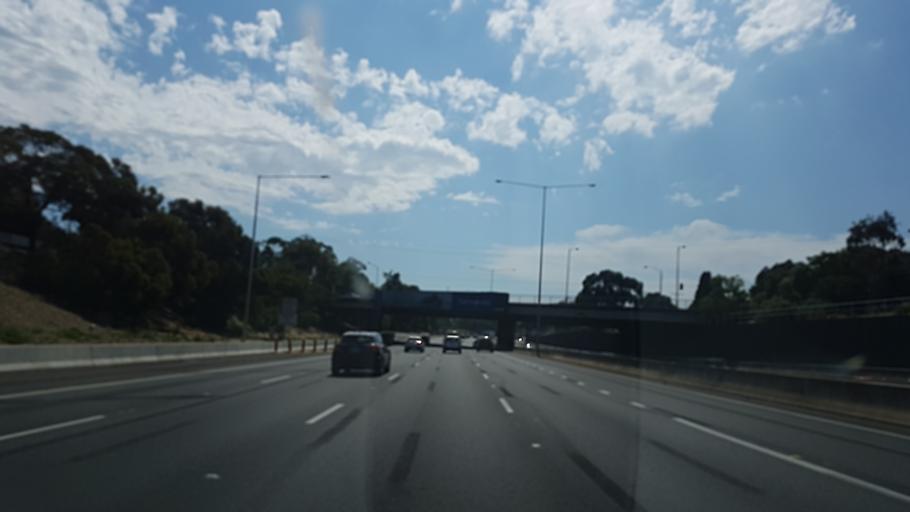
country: AU
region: Victoria
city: Brunswick West
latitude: -37.7531
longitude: 144.9361
